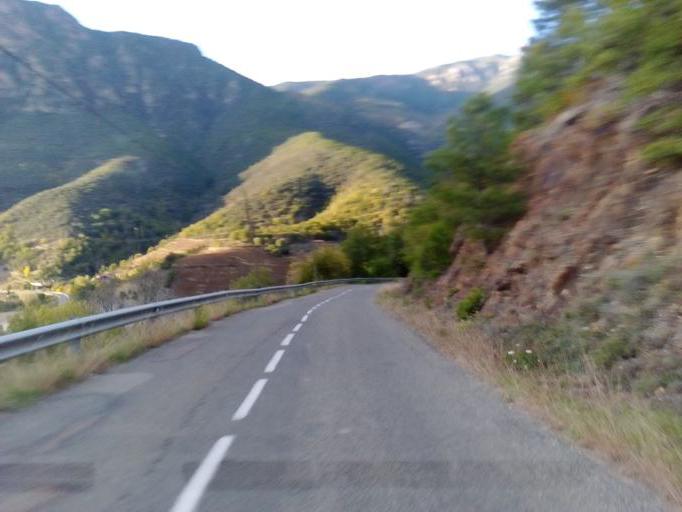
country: ES
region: Catalonia
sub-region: Provincia de Lleida
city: el Pont de Bar
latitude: 42.3542
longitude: 1.5821
